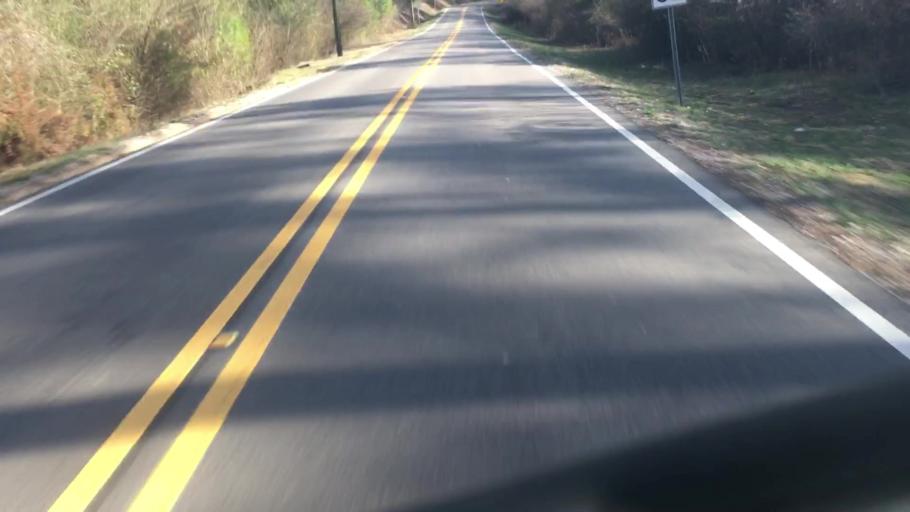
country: US
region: Alabama
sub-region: Shelby County
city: Brook Highland
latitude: 33.4568
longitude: -86.6959
